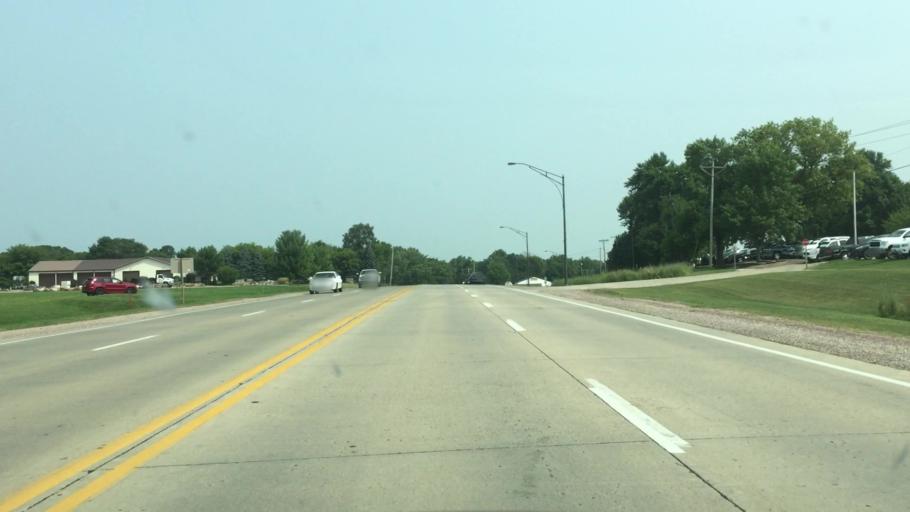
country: US
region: Iowa
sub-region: Dickinson County
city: Arnolds Park
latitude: 43.3575
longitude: -95.1420
